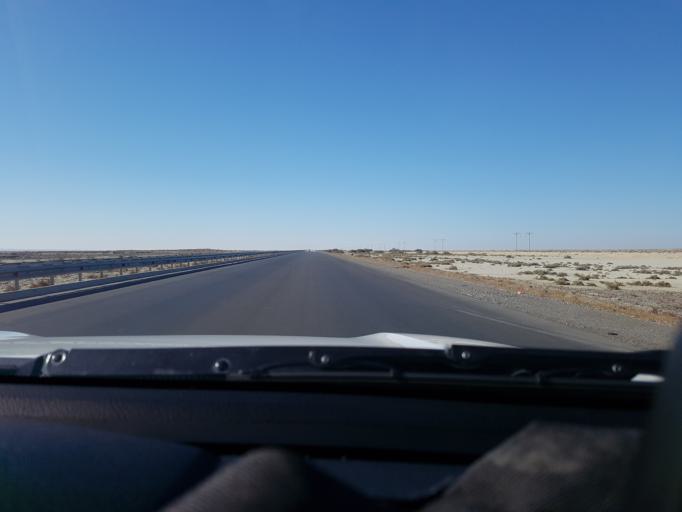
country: TM
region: Balkan
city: Gazanjyk
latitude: 39.2468
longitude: 55.0938
